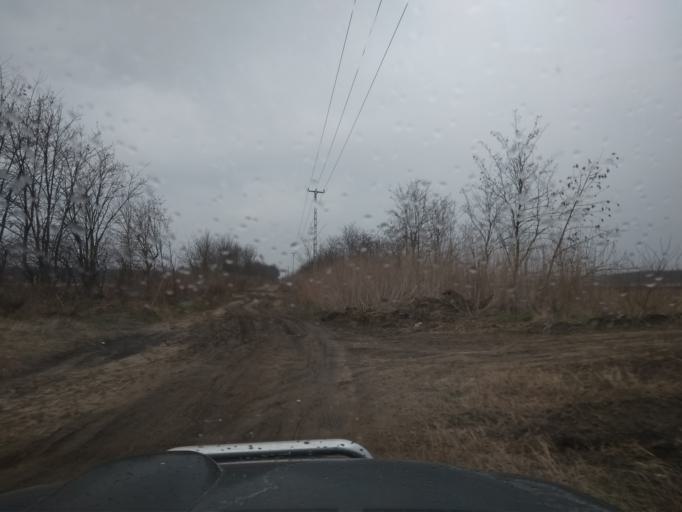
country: HU
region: Szabolcs-Szatmar-Bereg
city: Nyirpazony
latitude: 48.0081
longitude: 21.7887
